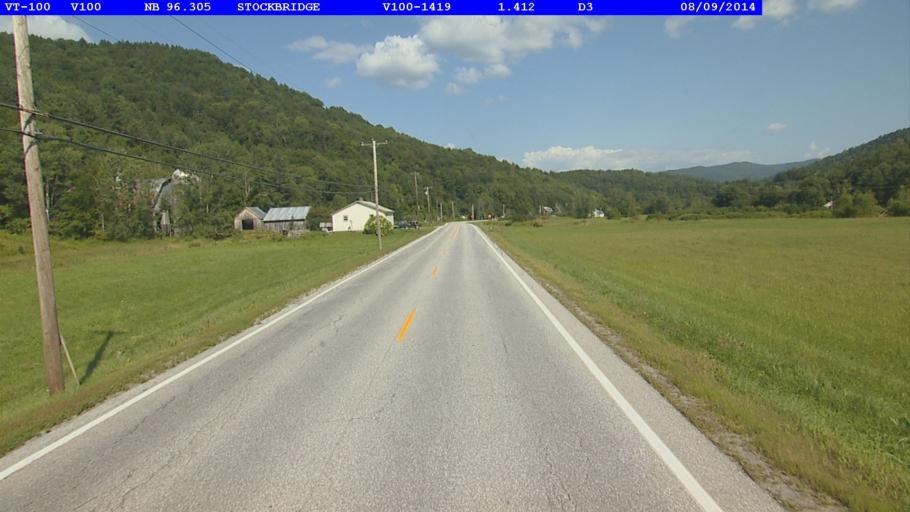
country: US
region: Vermont
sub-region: Orange County
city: Randolph
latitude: 43.7766
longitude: -72.7715
